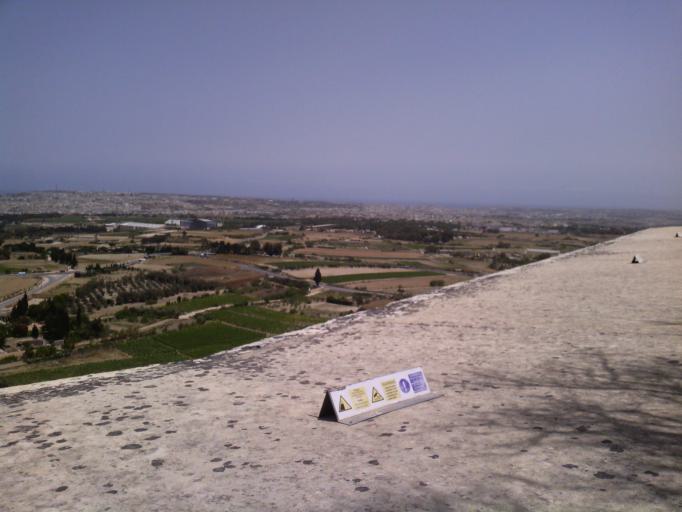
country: MT
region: L-Imdina
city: Imdina
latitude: 35.8876
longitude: 14.4030
